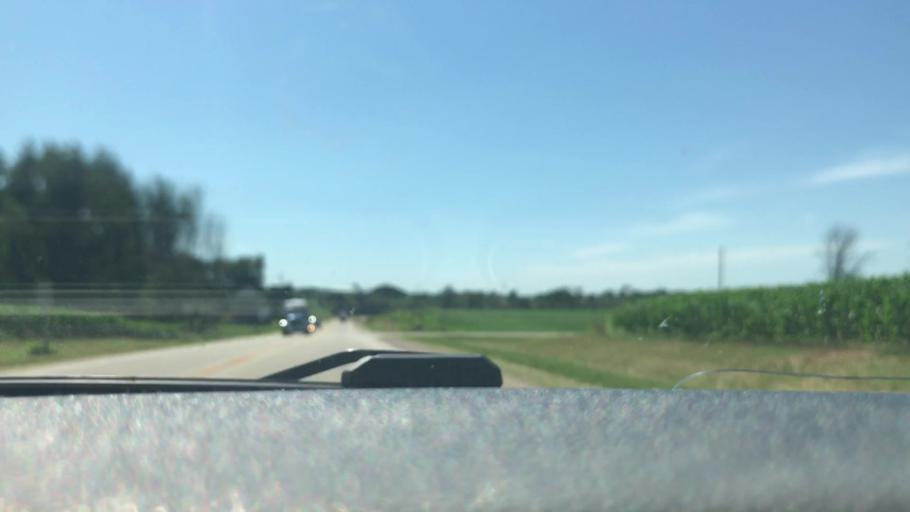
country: US
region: Wisconsin
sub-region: Washington County
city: Hartford
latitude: 43.4224
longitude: -88.3999
